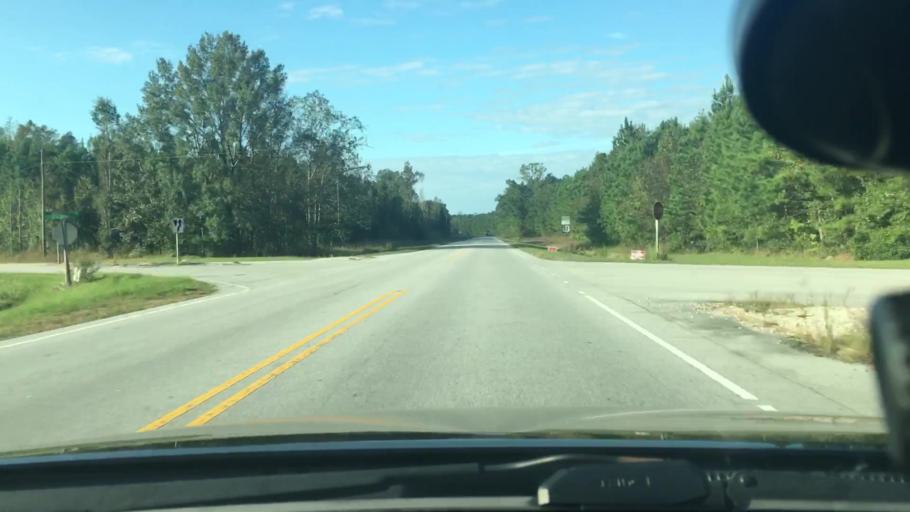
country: US
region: North Carolina
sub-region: Craven County
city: Vanceboro
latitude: 35.2949
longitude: -77.1305
